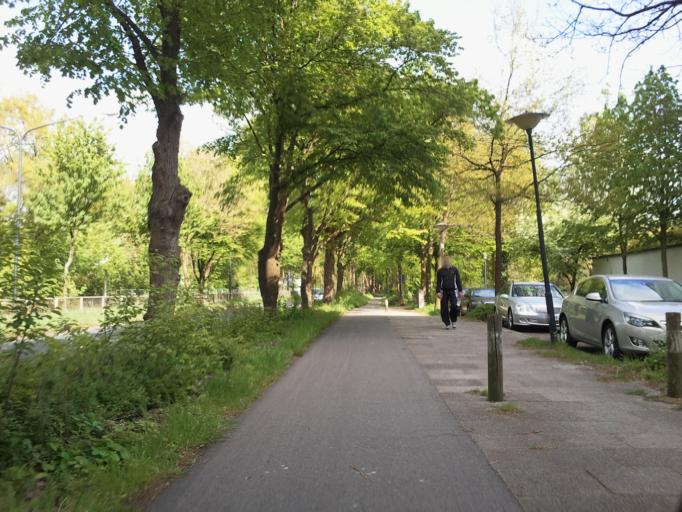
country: DE
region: Lower Saxony
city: Lilienthal
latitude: 53.0823
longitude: 8.8938
